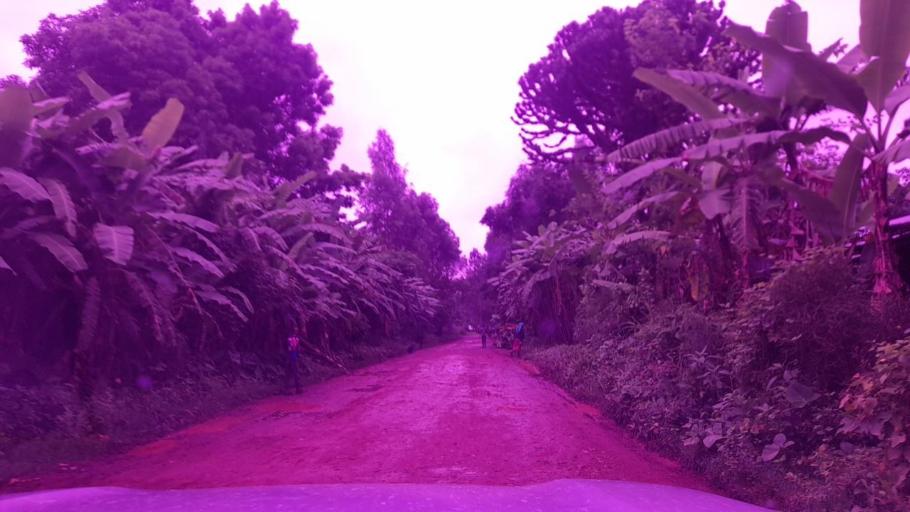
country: ET
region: Southern Nations, Nationalities, and People's Region
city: Bonga
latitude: 7.5774
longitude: 36.0331
